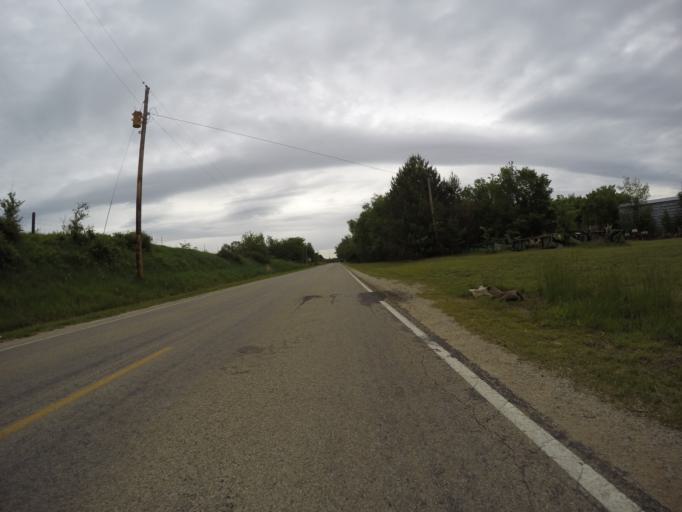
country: US
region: Kansas
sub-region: Pottawatomie County
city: Wamego
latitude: 39.1919
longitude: -96.3247
